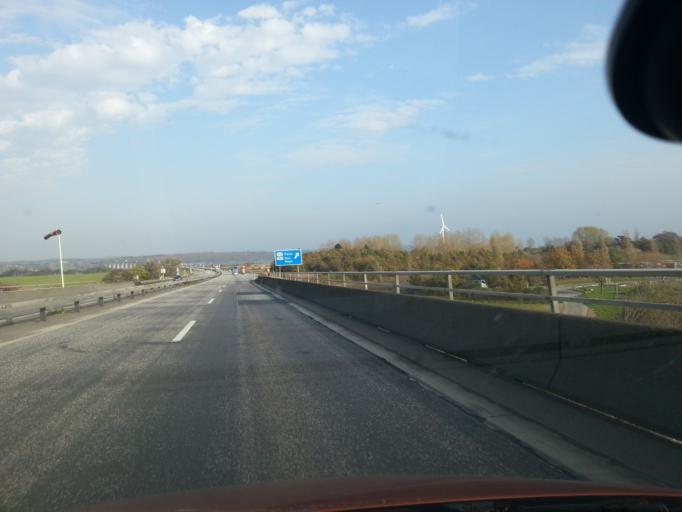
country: DK
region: Zealand
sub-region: Vordingborg Kommune
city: Nyrad
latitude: 54.9491
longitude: 11.9833
